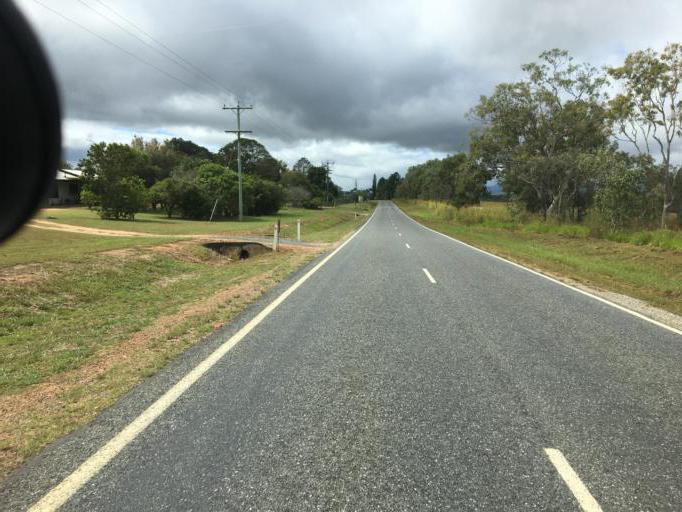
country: AU
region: Queensland
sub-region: Tablelands
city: Mareeba
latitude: -17.0157
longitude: 145.3584
